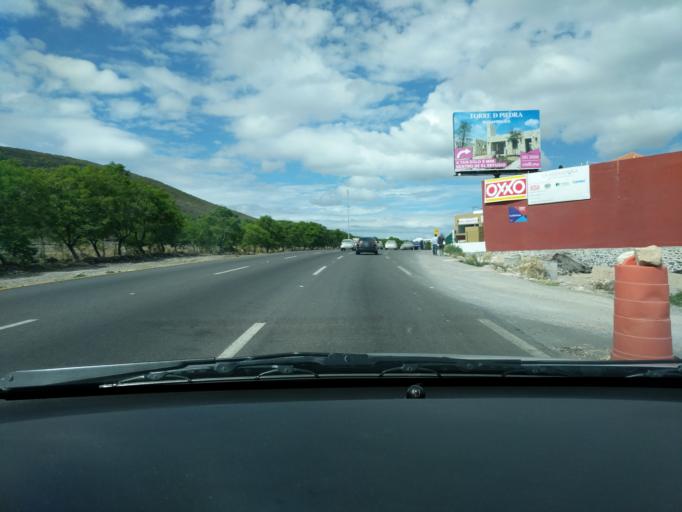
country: MX
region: Queretaro
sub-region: El Marques
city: La Pradera
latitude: 20.6607
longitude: -100.3505
